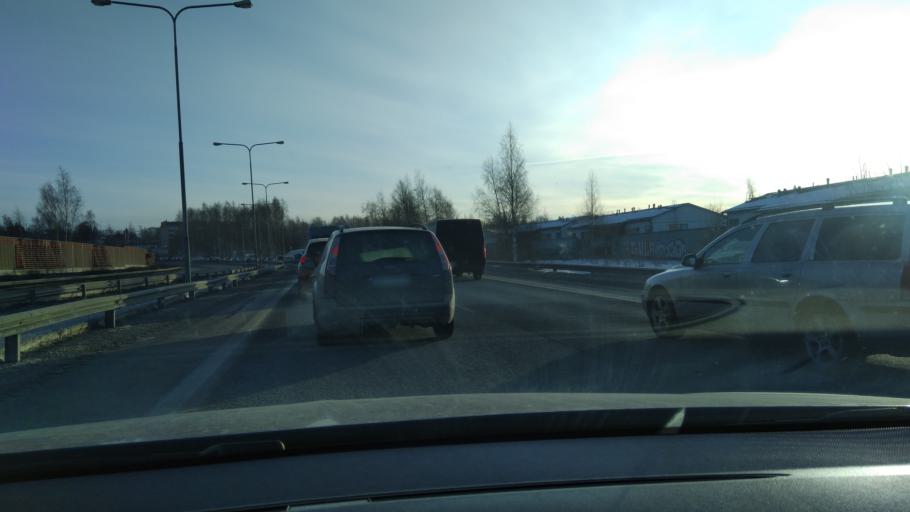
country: FI
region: Pirkanmaa
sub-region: Tampere
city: Pirkkala
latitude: 61.5050
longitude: 23.6828
